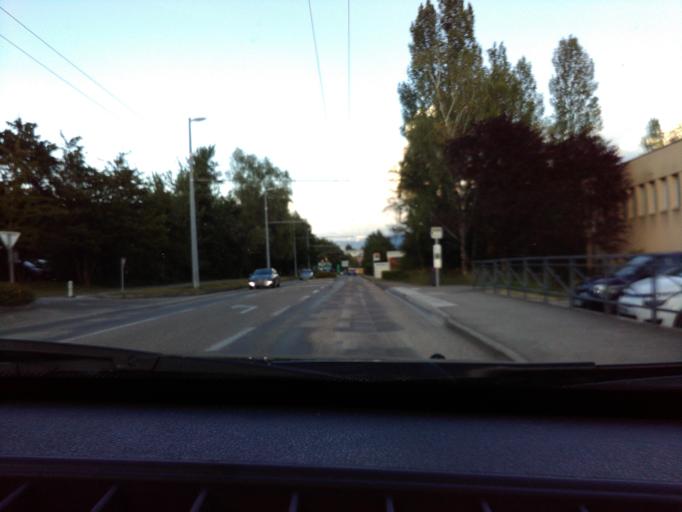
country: FR
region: Rhone-Alpes
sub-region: Departement de l'Isere
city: Meylan
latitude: 45.2103
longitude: 5.7843
